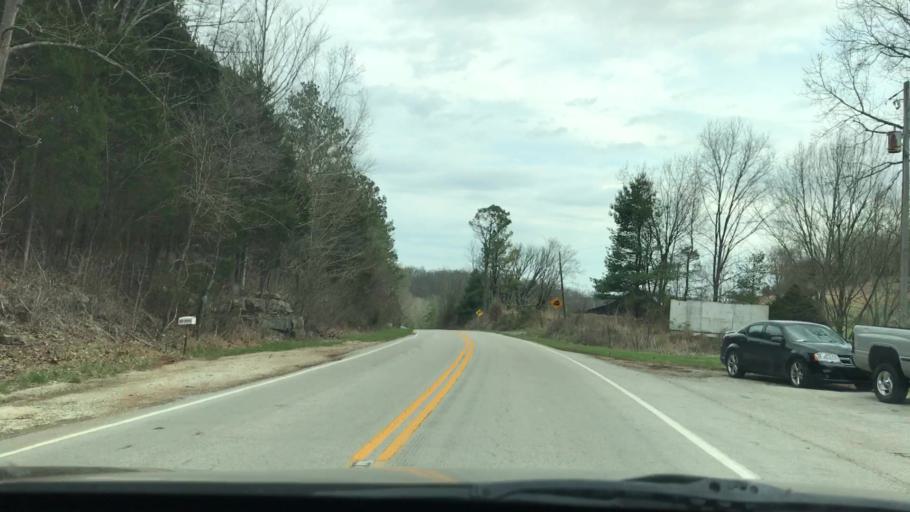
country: US
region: Kentucky
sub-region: Hart County
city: Munfordville
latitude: 37.3294
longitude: -85.7652
